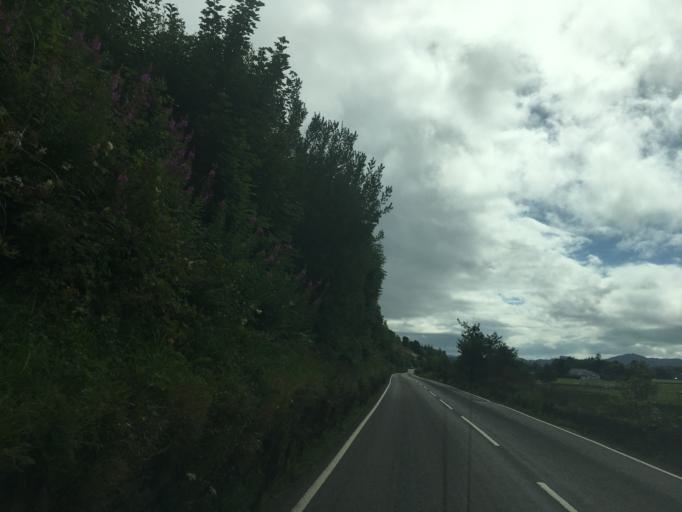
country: GB
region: Scotland
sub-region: Argyll and Bute
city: Lochgilphead
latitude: 56.1301
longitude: -5.4857
